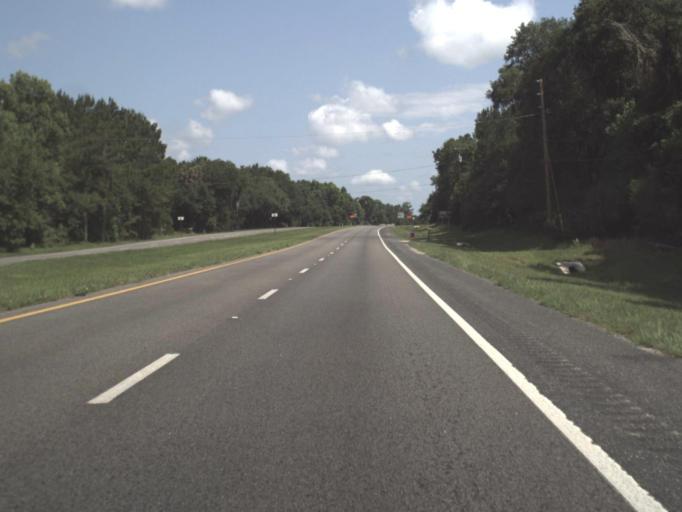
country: US
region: Florida
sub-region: Alachua County
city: Gainesville
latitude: 29.5543
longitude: -82.3287
